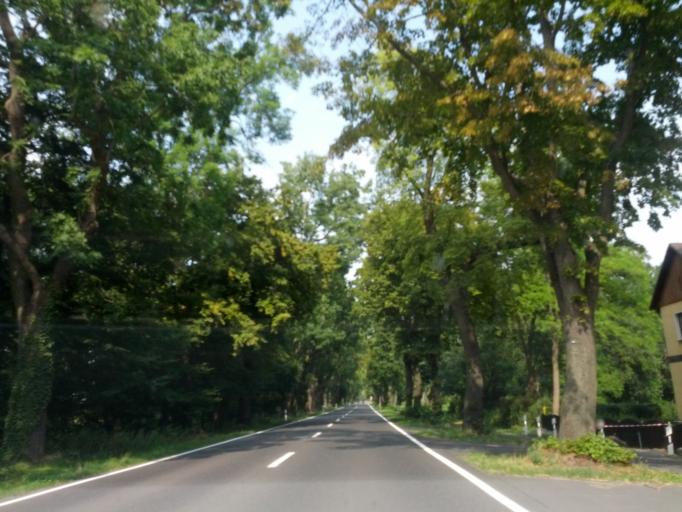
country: DE
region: Brandenburg
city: Nauen
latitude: 52.6195
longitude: 12.8911
